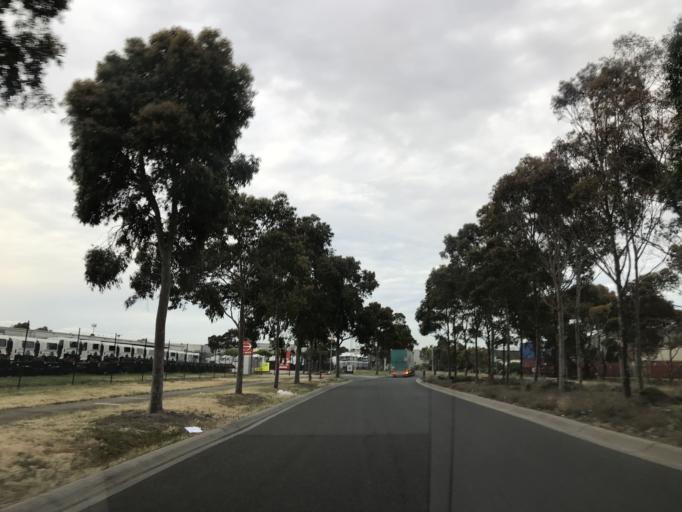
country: AU
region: Victoria
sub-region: Brimbank
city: Derrimut
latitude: -37.8125
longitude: 144.7823
